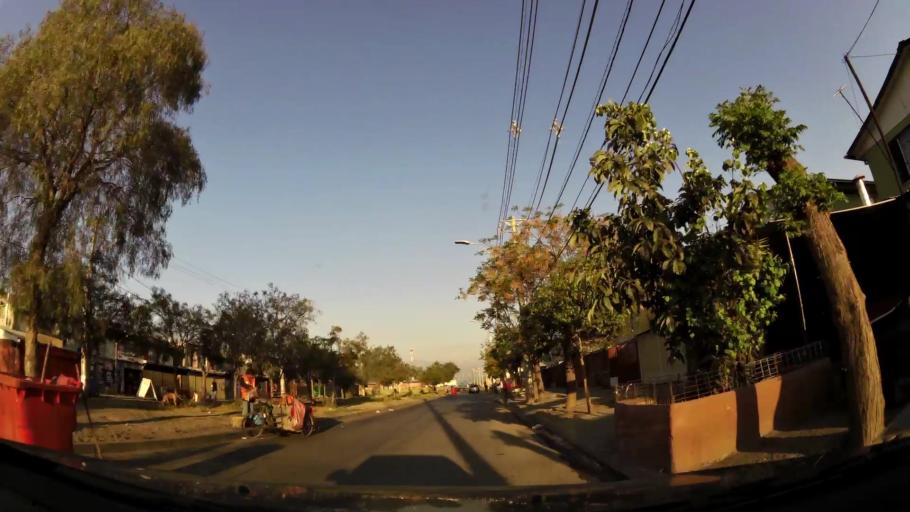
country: CL
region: Santiago Metropolitan
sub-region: Provincia de Maipo
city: San Bernardo
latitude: -33.5960
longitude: -70.6700
